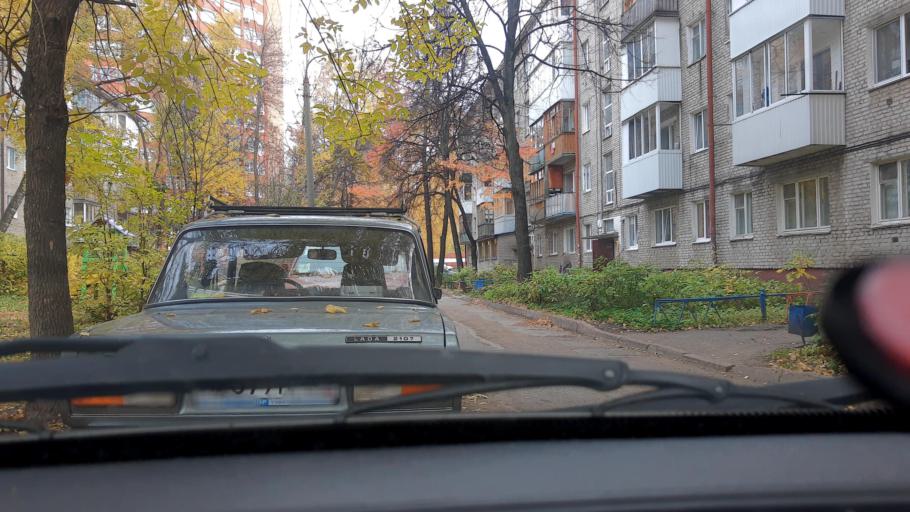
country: RU
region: Bashkortostan
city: Ufa
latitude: 54.7517
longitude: 55.9916
